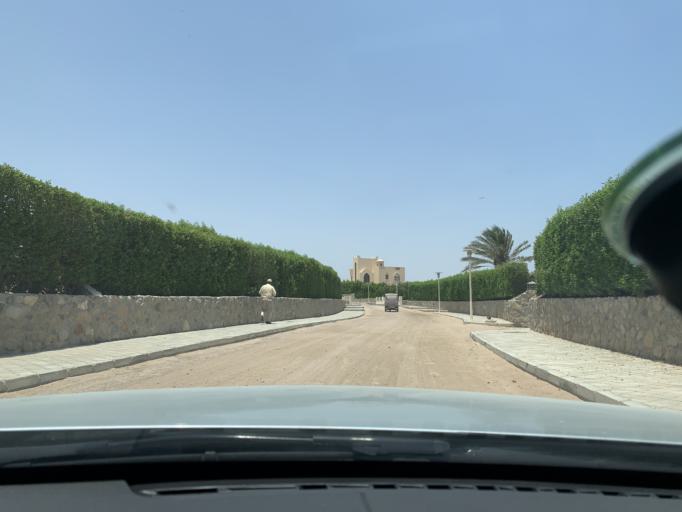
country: EG
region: Red Sea
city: El Gouna
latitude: 27.4142
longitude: 33.6696
